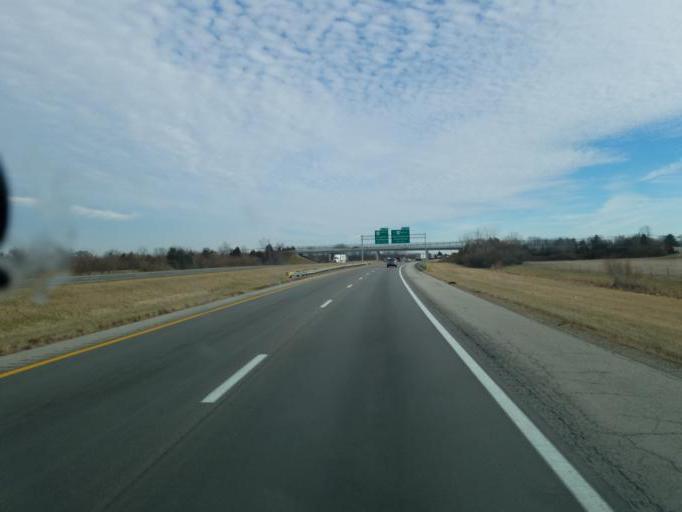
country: US
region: Ohio
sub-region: Montgomery County
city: Brookville
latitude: 39.8567
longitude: -84.4099
